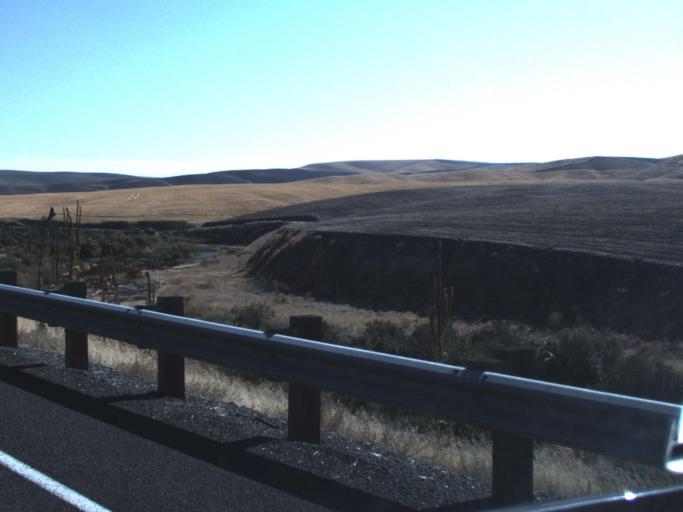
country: US
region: Washington
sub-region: Walla Walla County
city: Garrett
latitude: 46.2894
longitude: -118.5008
